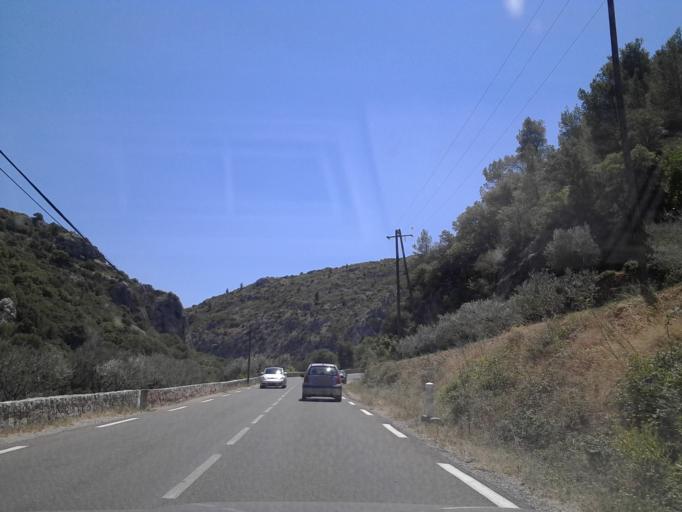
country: FR
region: Languedoc-Roussillon
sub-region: Departement de l'Herault
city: Saint-Jean-de-Fos
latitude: 43.7143
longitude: 3.5525
